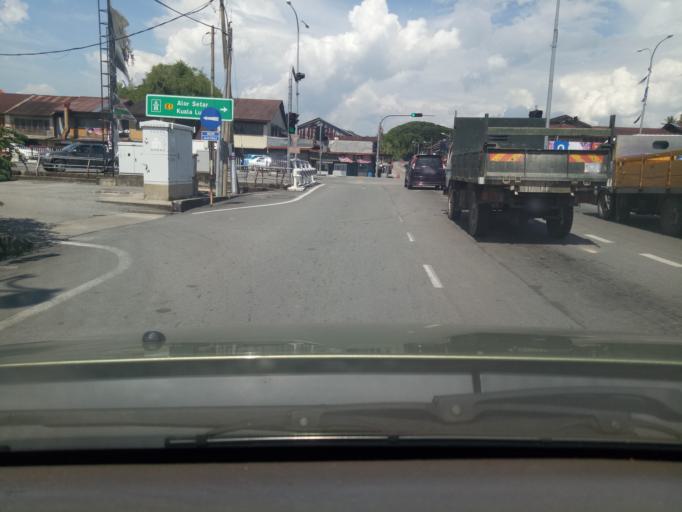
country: MY
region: Kedah
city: Gurun
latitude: 5.8585
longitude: 100.4566
